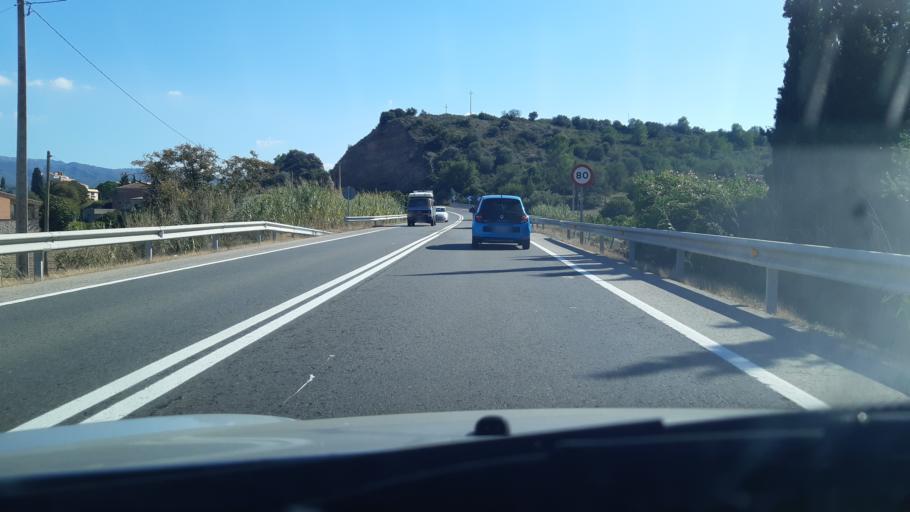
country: ES
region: Catalonia
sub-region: Provincia de Tarragona
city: Tivenys
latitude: 40.8835
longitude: 0.4941
